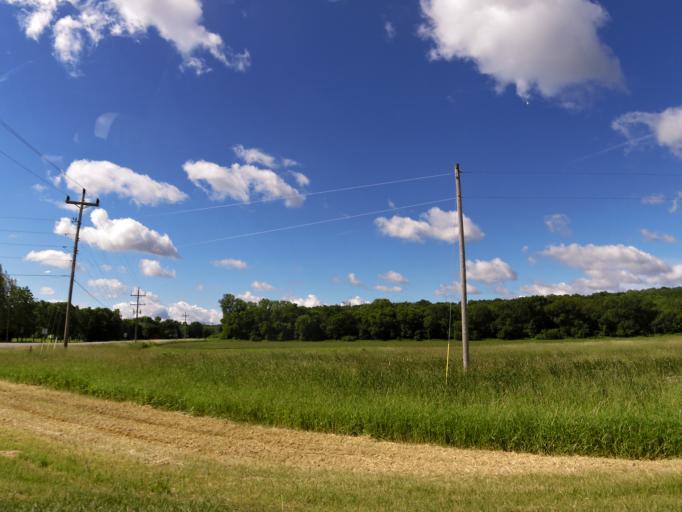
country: US
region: Minnesota
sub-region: Olmsted County
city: Rochester
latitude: 44.0100
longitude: -92.3793
